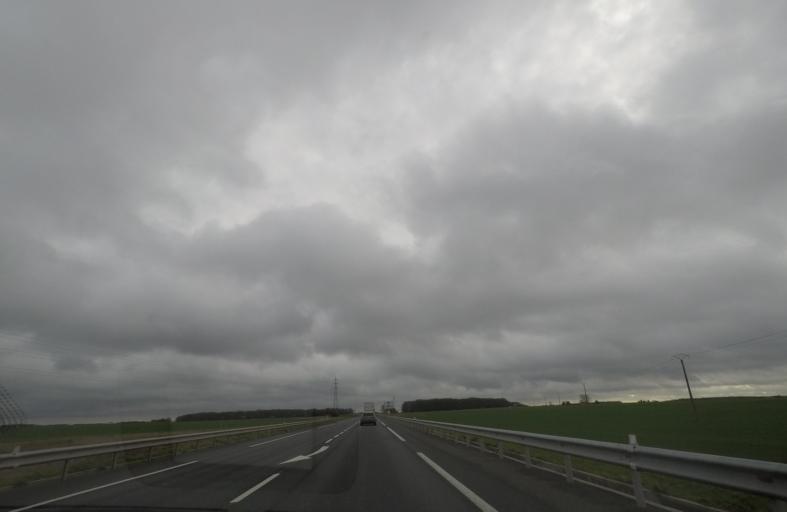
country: FR
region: Centre
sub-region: Departement du Loir-et-Cher
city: Vendome
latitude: 47.7678
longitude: 1.0687
